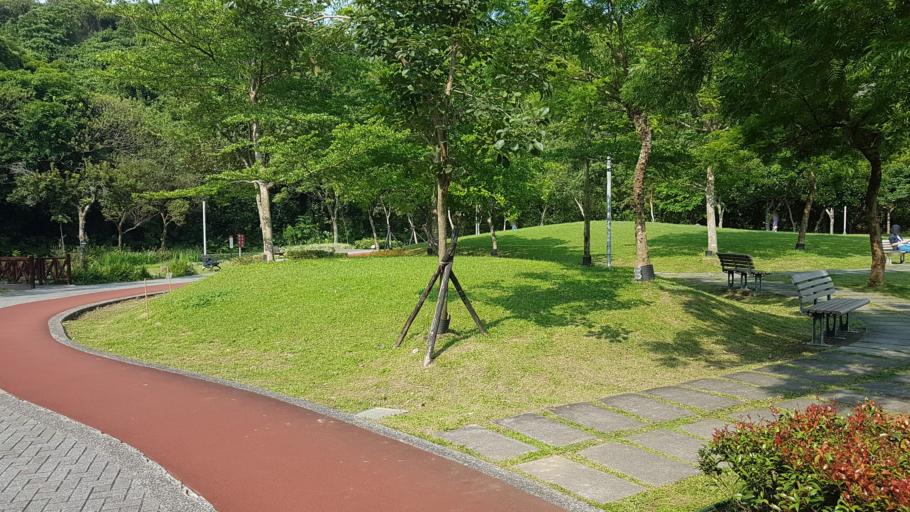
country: TW
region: Taipei
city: Taipei
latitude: 25.0030
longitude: 121.5438
